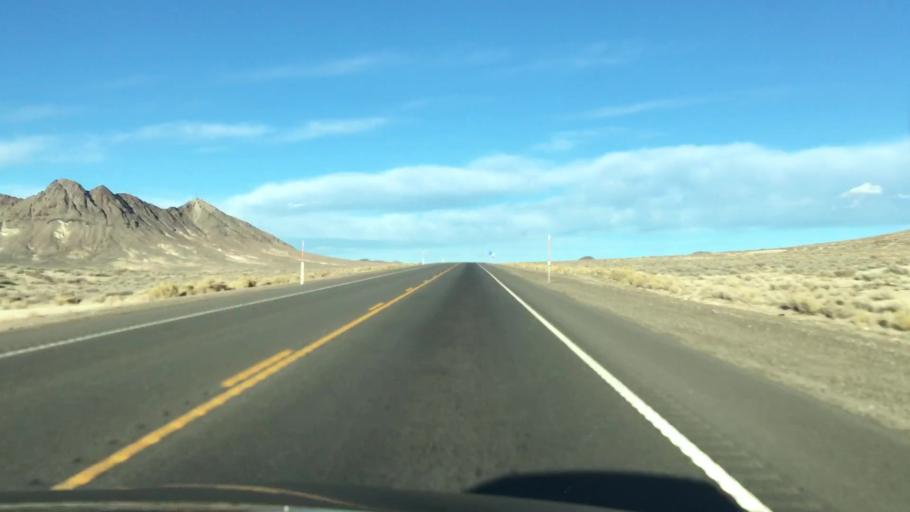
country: US
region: Nevada
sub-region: Nye County
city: Tonopah
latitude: 38.0219
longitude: -117.2435
